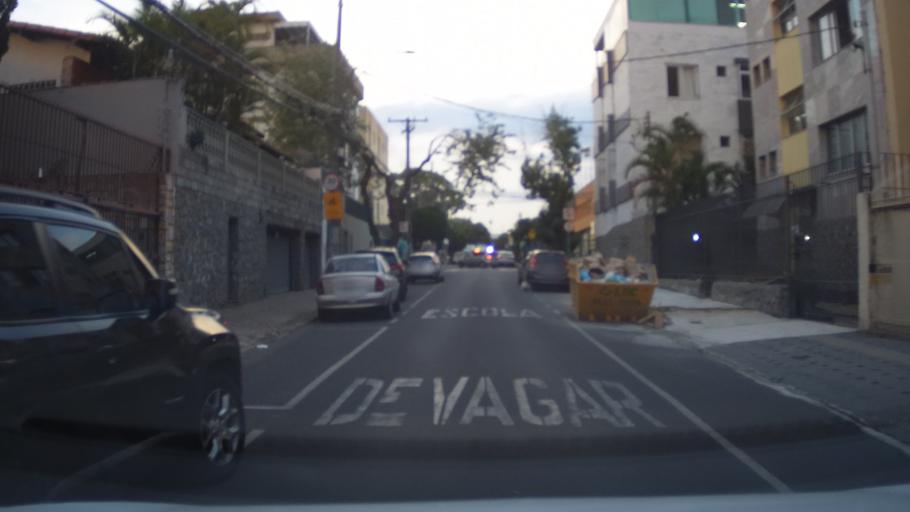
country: BR
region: Minas Gerais
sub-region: Belo Horizonte
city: Belo Horizonte
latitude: -19.8920
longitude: -43.9319
